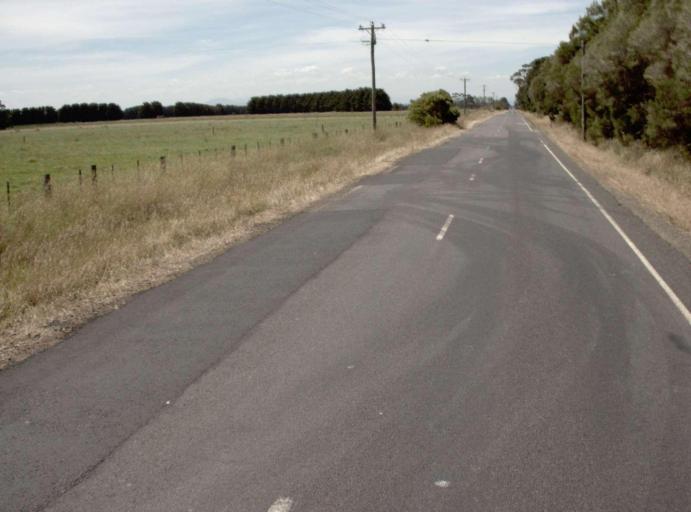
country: AU
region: Victoria
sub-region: Wellington
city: Heyfield
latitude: -38.0976
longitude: 146.8650
